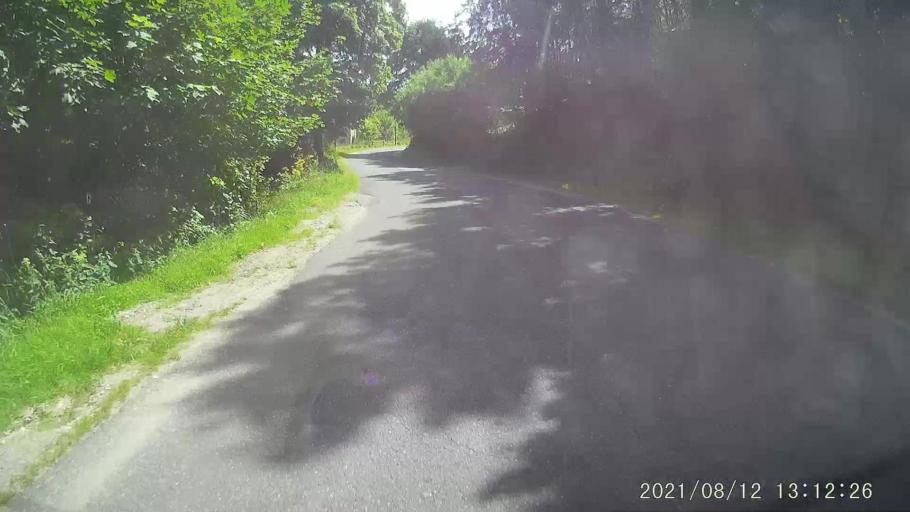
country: PL
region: Lower Silesian Voivodeship
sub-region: Powiat klodzki
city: Stronie Slaskie
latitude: 50.2473
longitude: 16.8518
